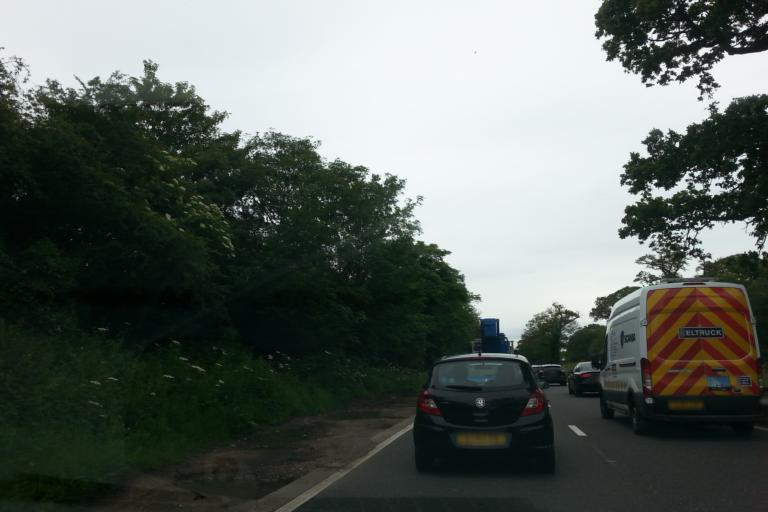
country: GB
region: England
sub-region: Solihull
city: Bickenhill
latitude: 52.4638
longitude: -1.7039
